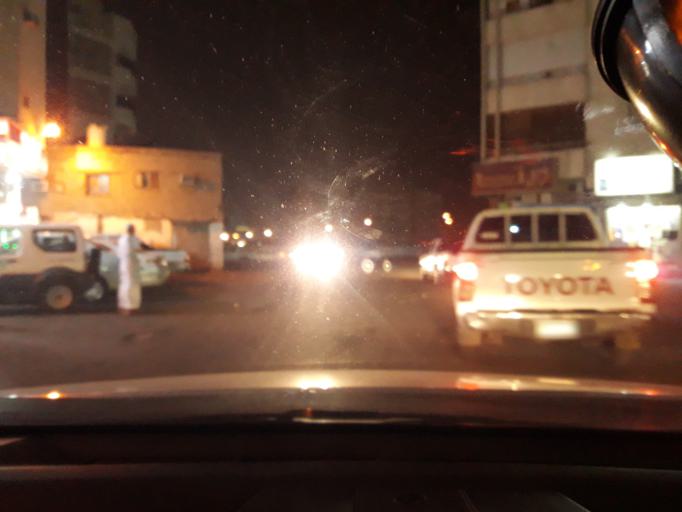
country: SA
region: Al Madinah al Munawwarah
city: Medina
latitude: 24.4673
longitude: 39.6273
